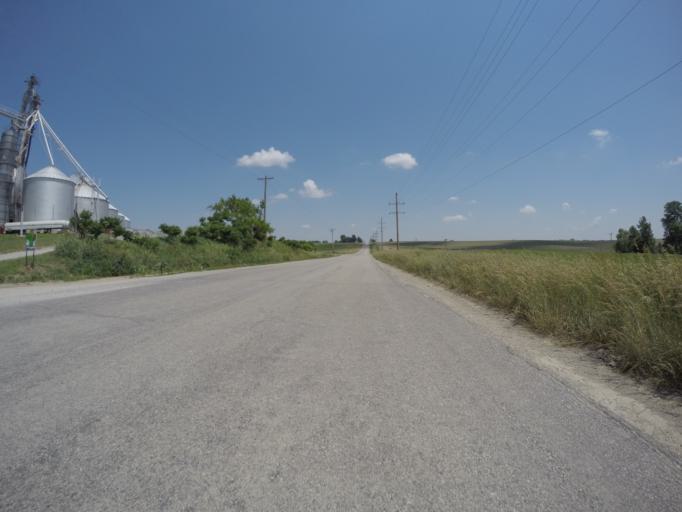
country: US
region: Kansas
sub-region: Doniphan County
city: Troy
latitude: 39.7689
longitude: -95.1163
